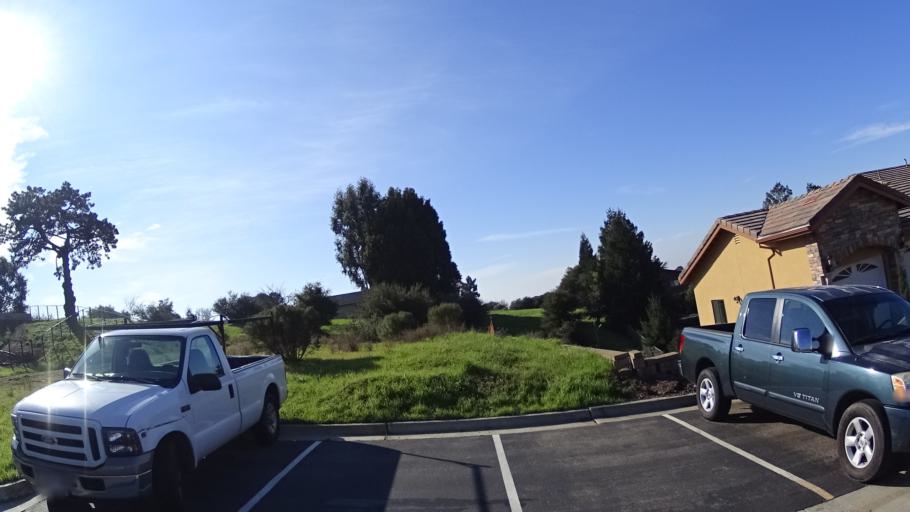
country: US
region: California
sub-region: Alameda County
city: Fairview
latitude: 37.6771
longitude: -122.0459
